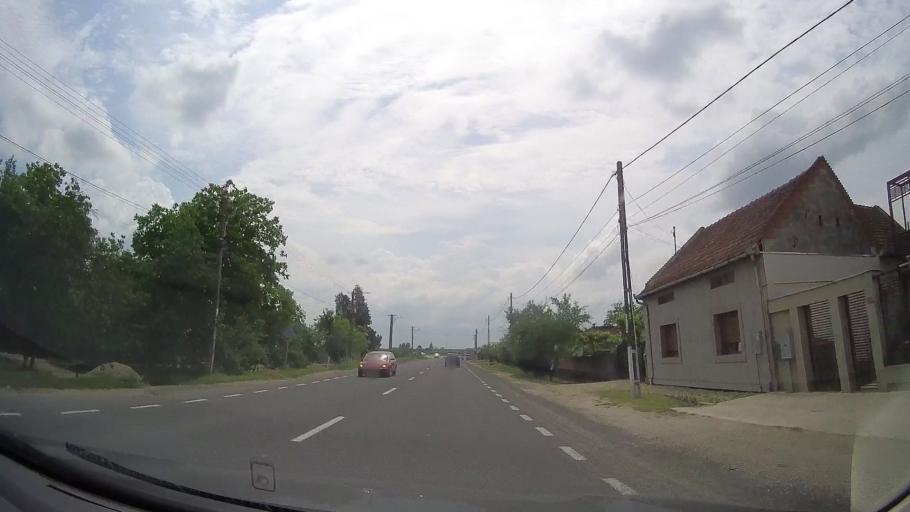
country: RO
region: Timis
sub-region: Comuna Costeiu
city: Costeiu
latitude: 45.7292
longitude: 21.8690
